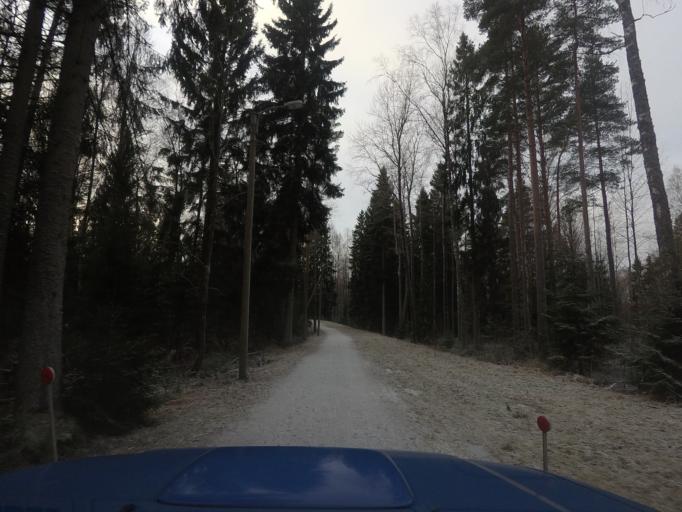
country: FI
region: Uusimaa
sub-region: Helsinki
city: Espoo
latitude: 60.1846
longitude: 24.6530
